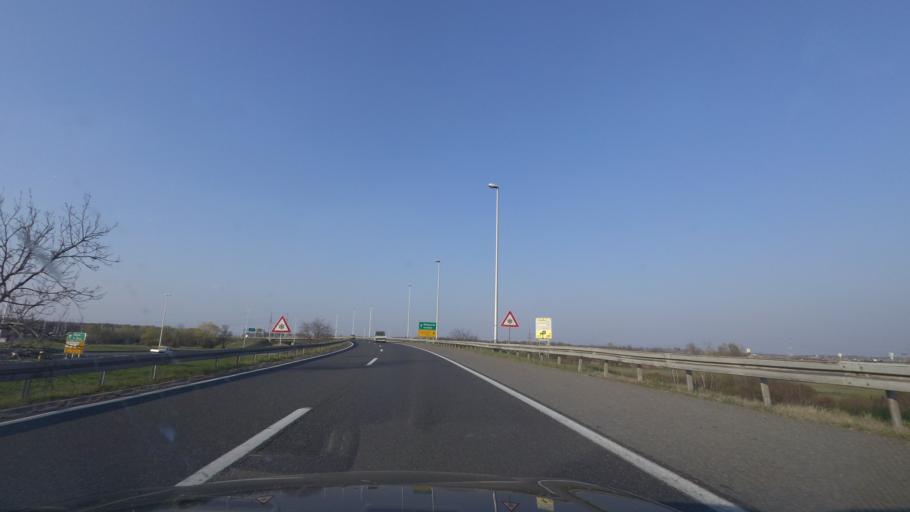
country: HR
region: Grad Zagreb
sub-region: Sesvete
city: Sesvete
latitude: 45.7932
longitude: 16.1297
